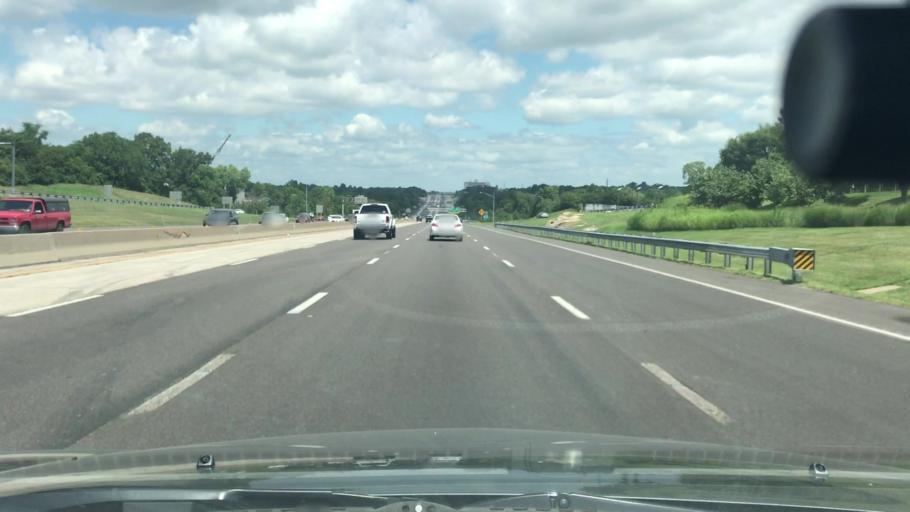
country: US
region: Missouri
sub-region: Saint Louis County
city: Creve Coeur
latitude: 38.6734
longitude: -90.4491
